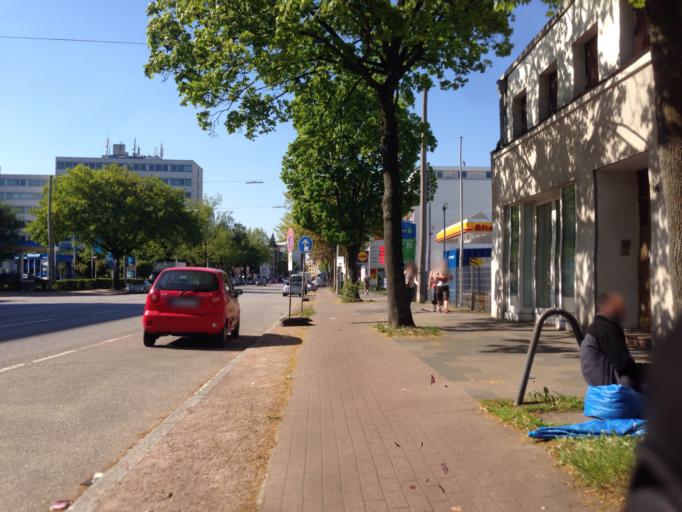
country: DE
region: Hamburg
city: Hamburg
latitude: 53.5734
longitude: 10.0236
